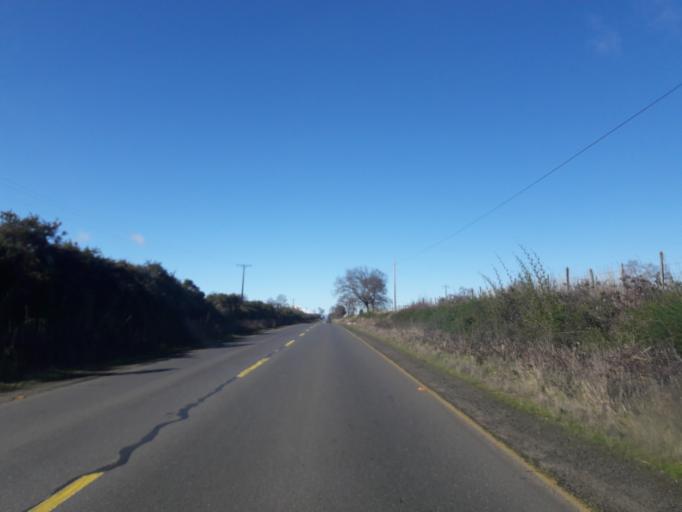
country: CL
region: Araucania
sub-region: Provincia de Malleco
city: Victoria
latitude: -38.2593
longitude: -72.2564
